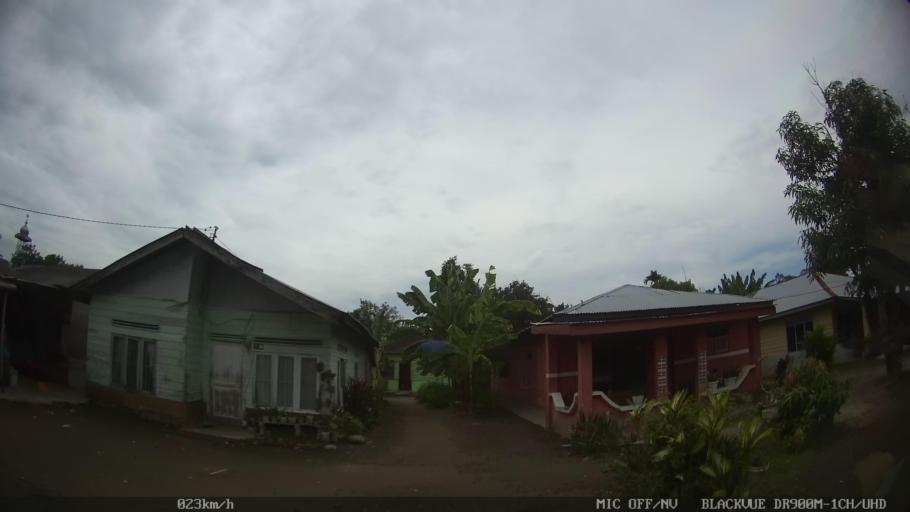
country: ID
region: North Sumatra
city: Sunggal
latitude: 3.6319
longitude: 98.5907
